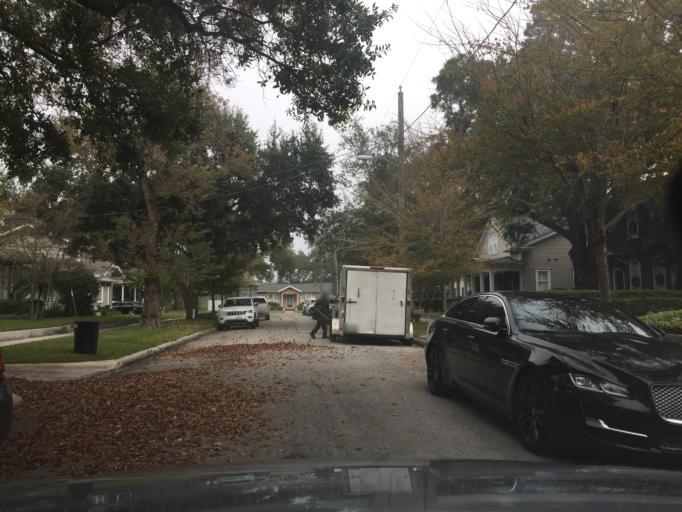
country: US
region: Florida
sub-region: Hillsborough County
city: Tampa
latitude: 27.9353
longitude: -82.4789
